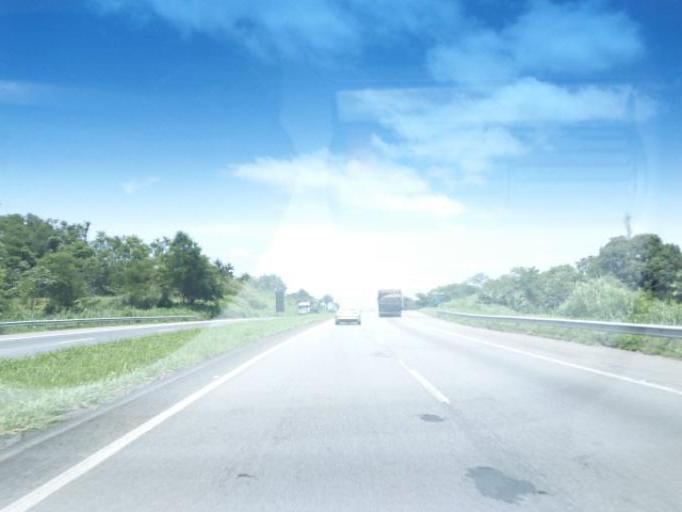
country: BR
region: Sao Paulo
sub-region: Miracatu
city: Miracatu
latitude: -24.3094
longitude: -47.5054
